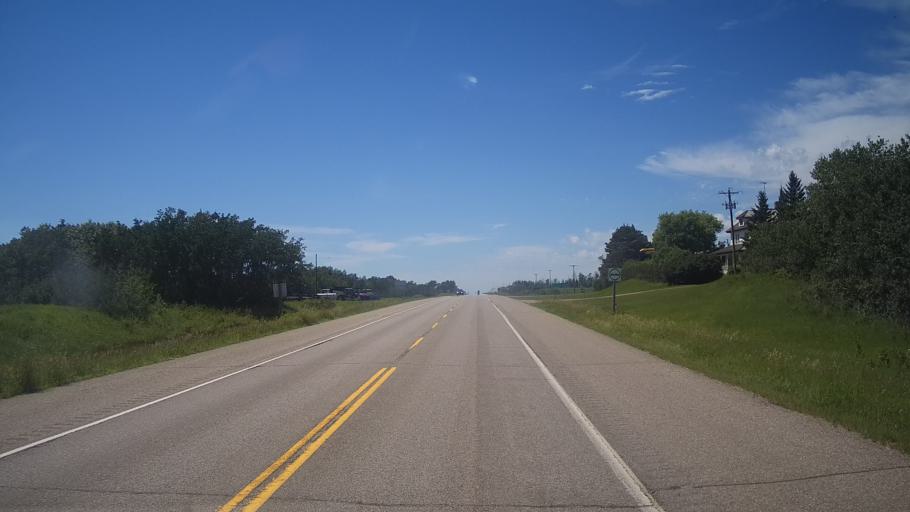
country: CA
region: Saskatchewan
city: Langenburg
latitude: 50.7715
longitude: -101.3013
